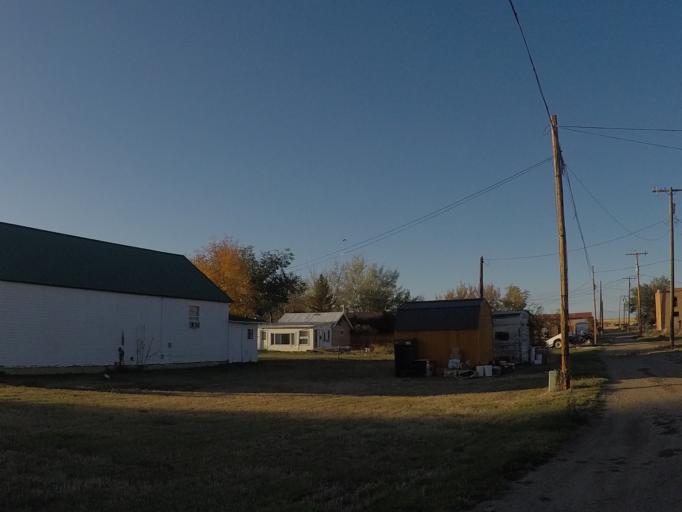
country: US
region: Montana
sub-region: Golden Valley County
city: Ryegate
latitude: 46.2936
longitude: -108.9387
